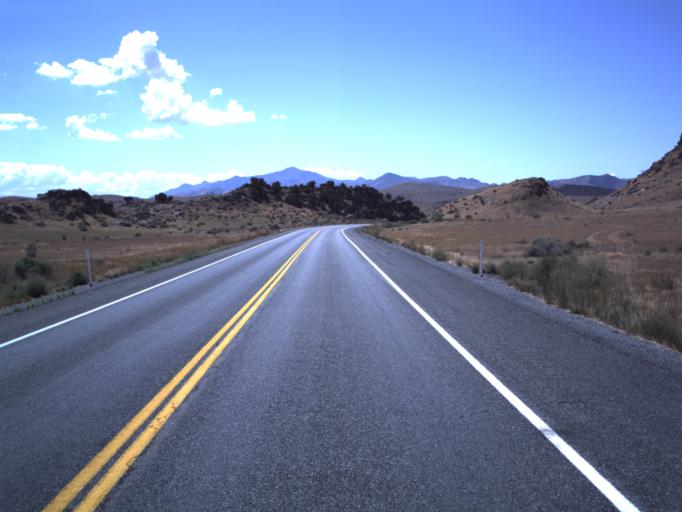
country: US
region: Utah
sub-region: Juab County
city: Nephi
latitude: 39.6471
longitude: -112.0807
